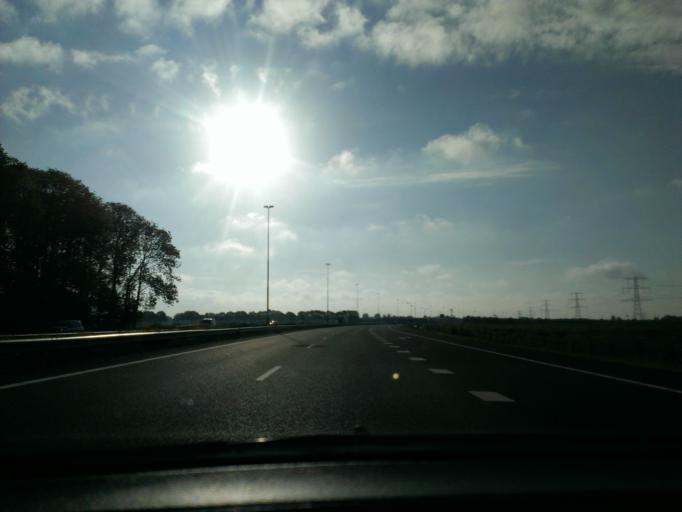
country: NL
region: Drenthe
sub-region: Gemeente Coevorden
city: Dalen
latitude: 52.7301
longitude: 6.7763
